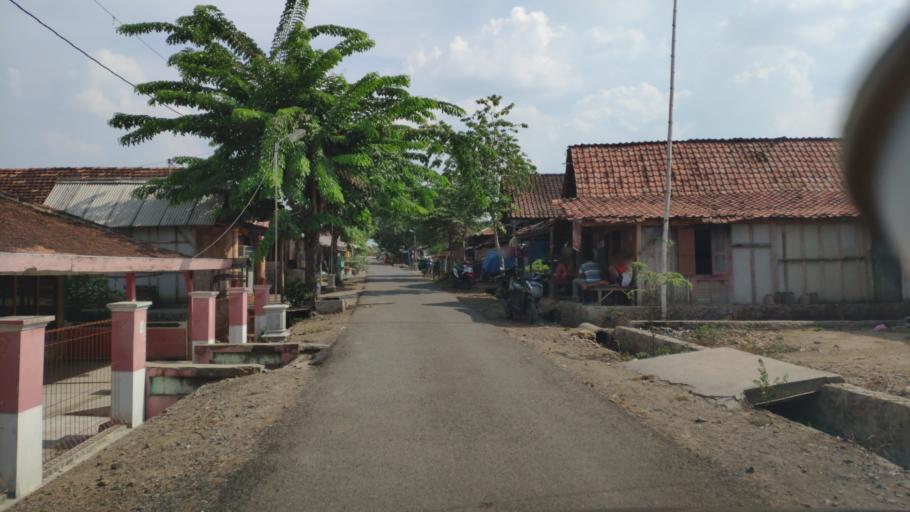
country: ID
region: Central Java
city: Plosorejo
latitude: -6.9925
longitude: 111.2613
